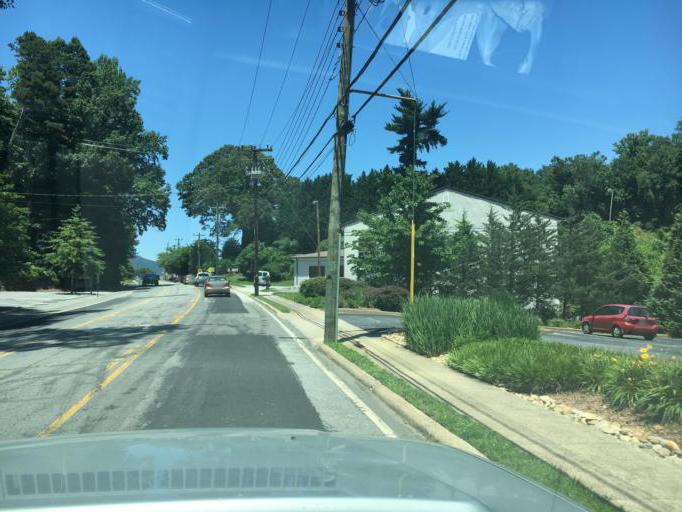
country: US
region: North Carolina
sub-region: Polk County
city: Tryon
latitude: 35.2051
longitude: -82.2374
